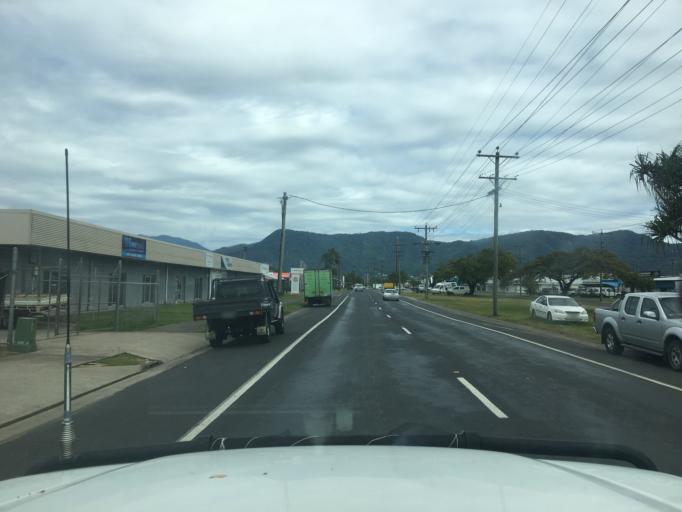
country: AU
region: Queensland
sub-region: Cairns
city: Woree
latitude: -16.9398
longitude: 145.7615
